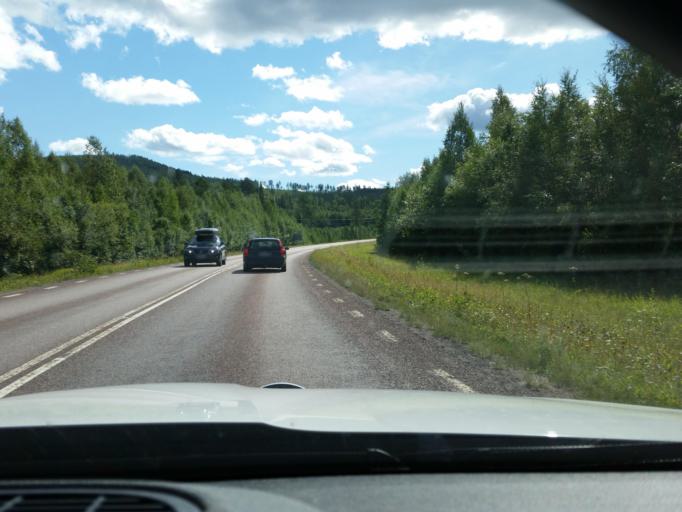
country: SE
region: Norrbotten
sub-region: Alvsbyns Kommun
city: AElvsbyn
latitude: 65.6748
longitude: 21.2087
